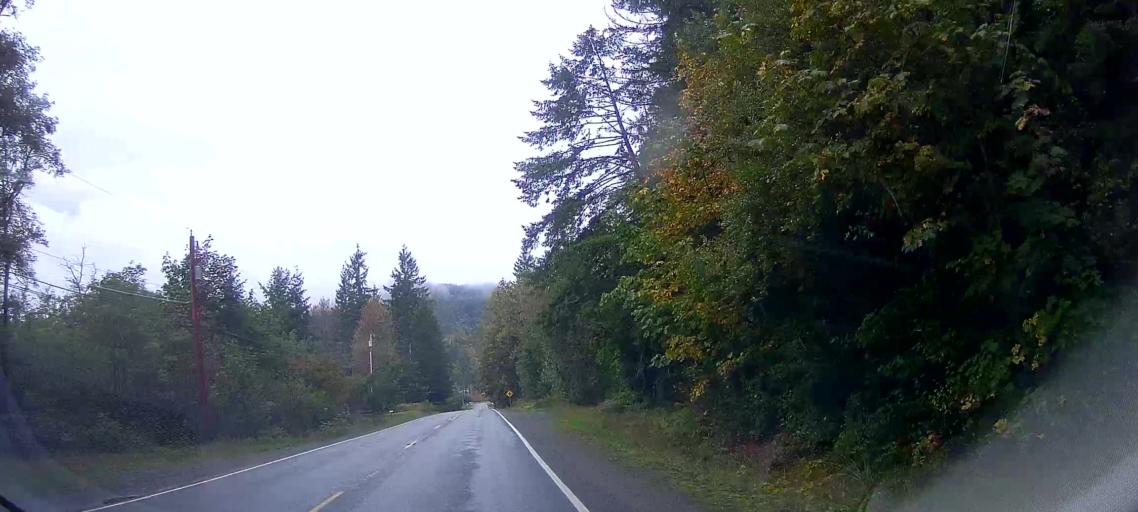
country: US
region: Washington
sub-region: Snohomish County
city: Darrington
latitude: 48.5323
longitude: -121.7661
